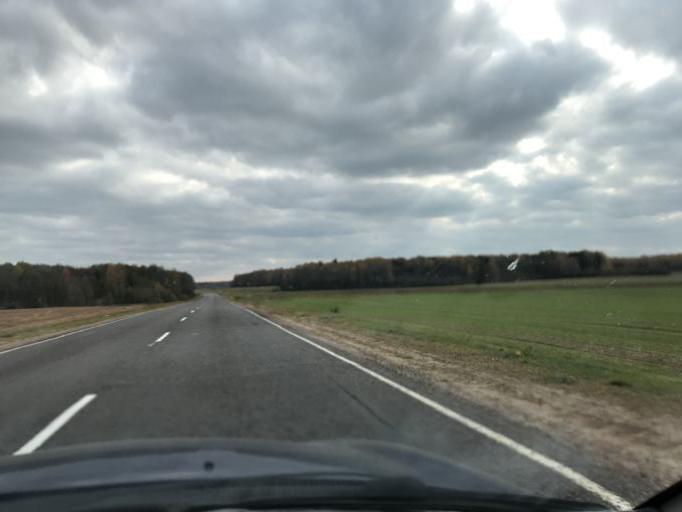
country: BY
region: Grodnenskaya
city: Lida
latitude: 53.7641
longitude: 25.1817
